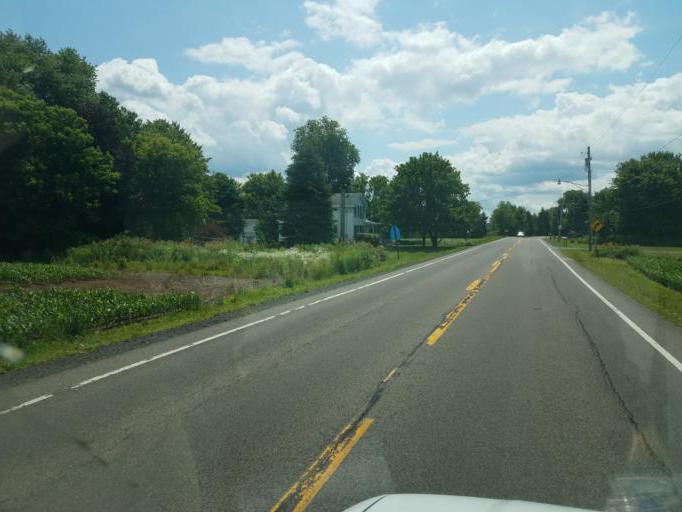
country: US
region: New York
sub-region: Wayne County
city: Clyde
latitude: 43.1494
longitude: -76.8767
